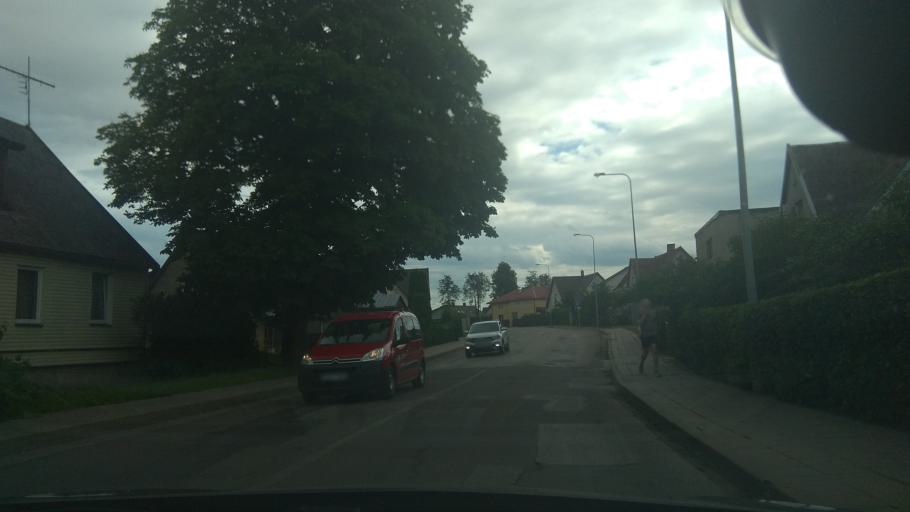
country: LT
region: Marijampoles apskritis
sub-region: Marijampole Municipality
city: Marijampole
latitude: 54.5508
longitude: 23.3531
